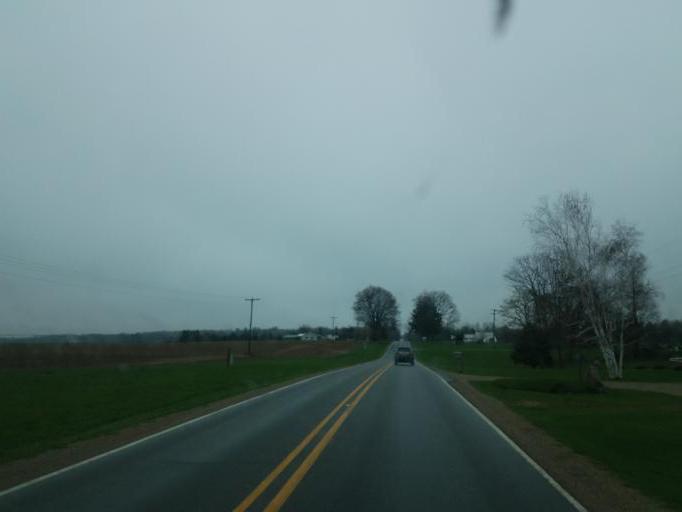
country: US
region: Michigan
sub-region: Isabella County
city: Lake Isabella
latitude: 43.5239
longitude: -85.0047
